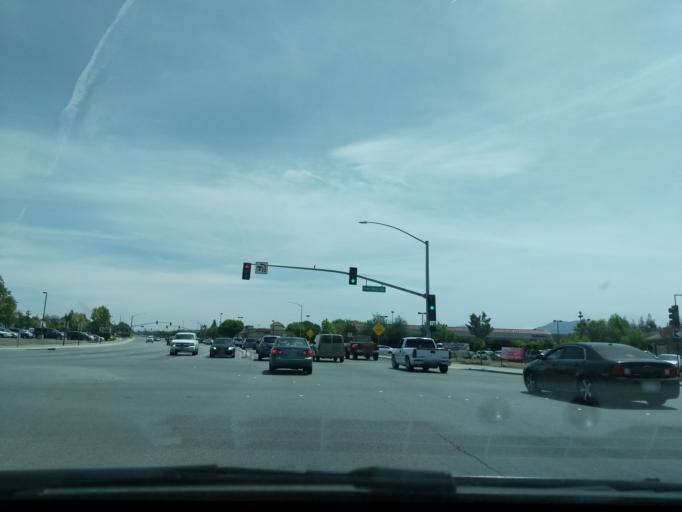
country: US
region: California
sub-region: San Benito County
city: Hollister
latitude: 36.8395
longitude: -121.3909
